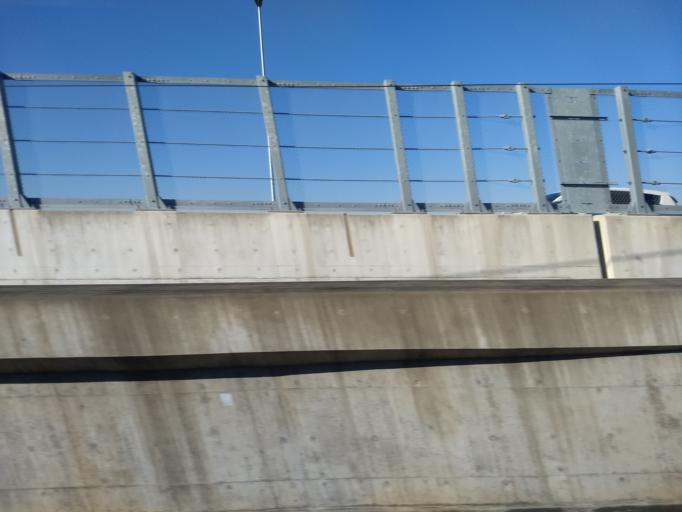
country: JP
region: Chiba
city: Narita
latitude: 35.7944
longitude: 140.2635
